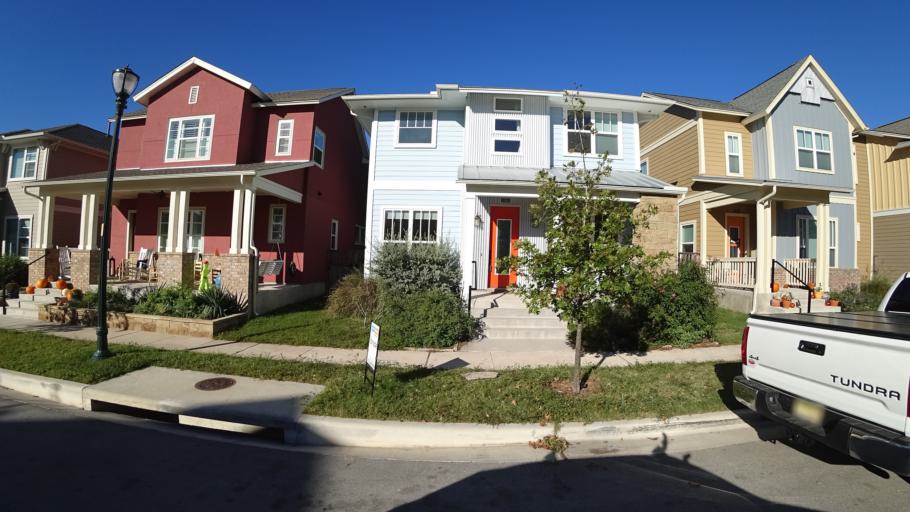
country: US
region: Texas
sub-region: Travis County
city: Austin
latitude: 30.2916
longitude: -97.6966
